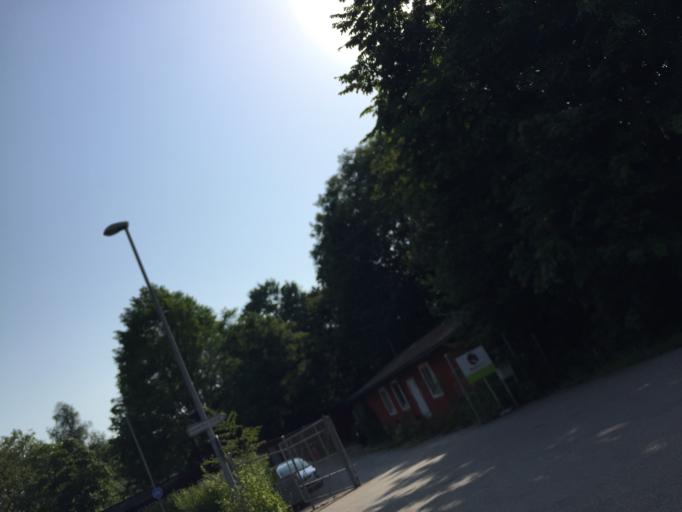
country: CH
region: Bern
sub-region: Bern-Mittelland District
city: Bolligen
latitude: 46.9626
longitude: 7.4768
